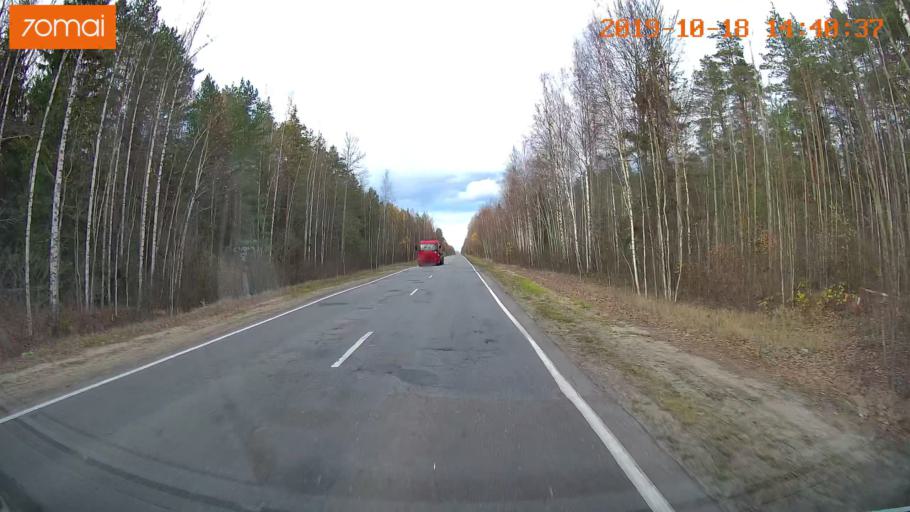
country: RU
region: Vladimir
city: Velikodvorskiy
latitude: 55.2793
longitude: 40.6694
